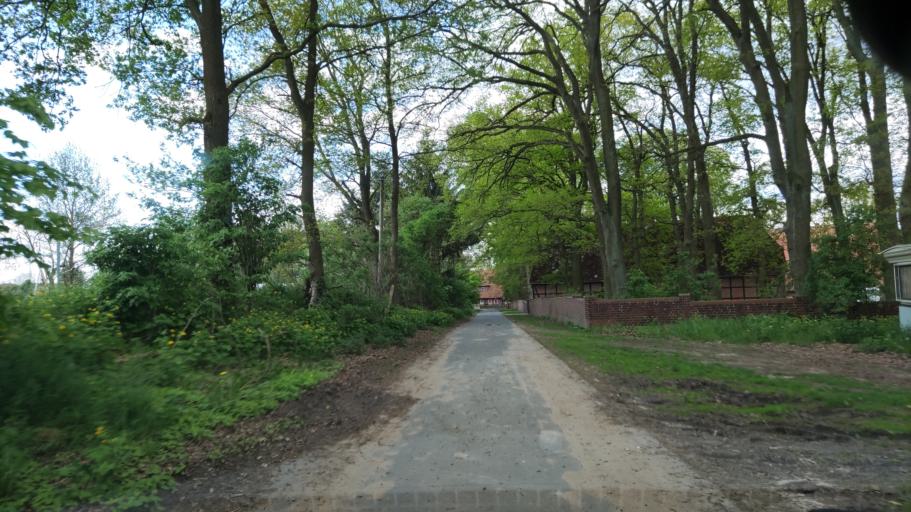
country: DE
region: Lower Saxony
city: Boitze
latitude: 53.1609
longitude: 10.7351
